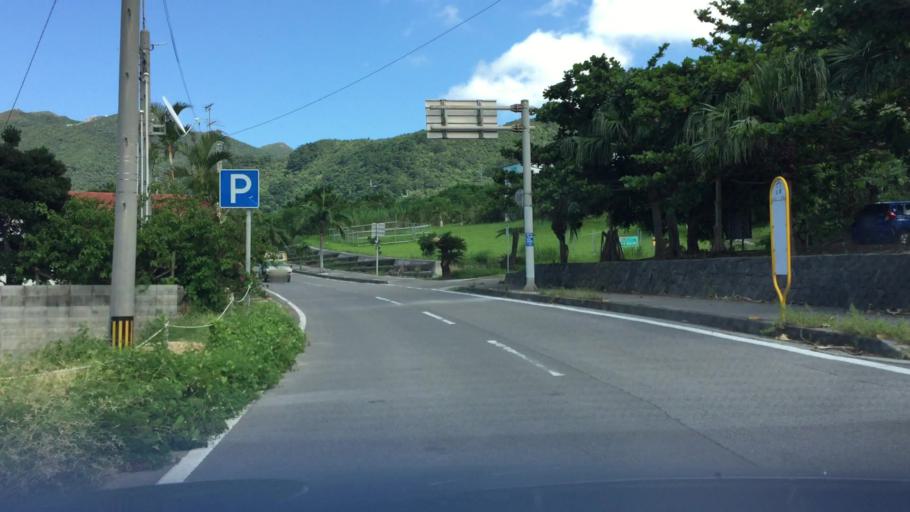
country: JP
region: Okinawa
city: Ishigaki
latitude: 24.4481
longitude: 124.1681
